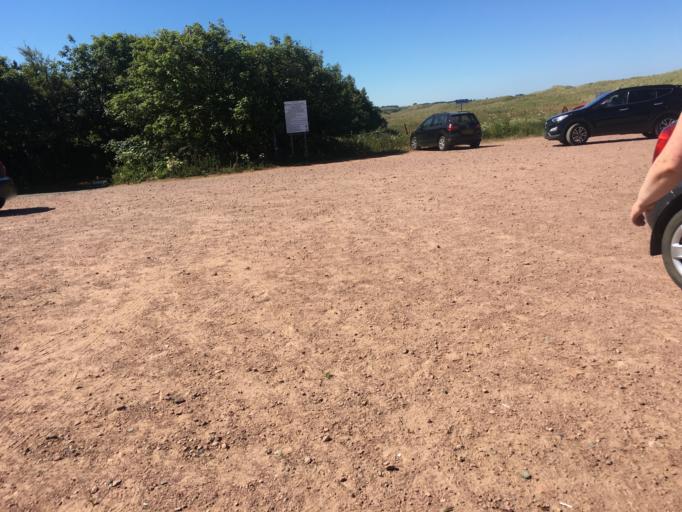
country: GB
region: England
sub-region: Northumberland
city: Beadnell
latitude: 55.5274
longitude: -1.6284
